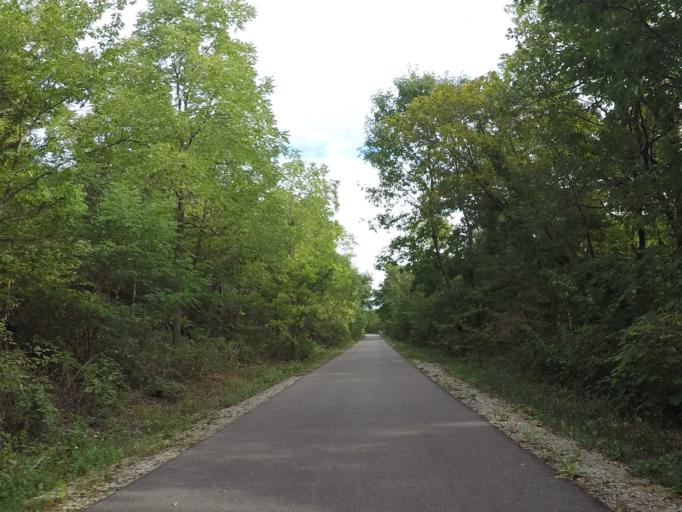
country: US
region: Wisconsin
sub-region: Sauk County
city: Prairie du Sac
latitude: 43.3031
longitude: -89.7310
